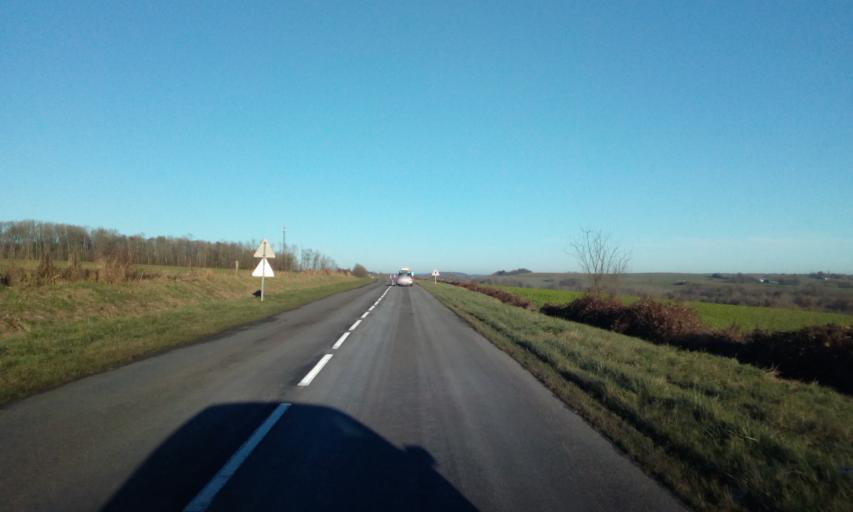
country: FR
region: Champagne-Ardenne
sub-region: Departement des Ardennes
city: Signy-le-Petit
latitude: 49.7485
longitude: 4.3050
